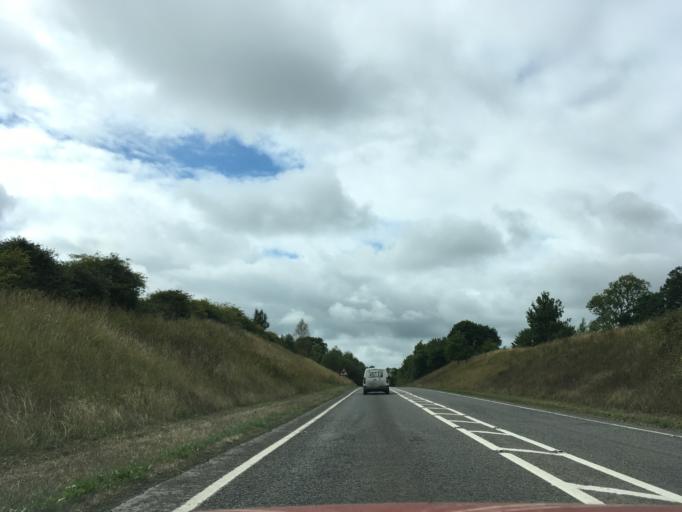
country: GB
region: Wales
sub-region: Carmarthenshire
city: Llandeilo
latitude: 51.8913
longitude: -4.0155
